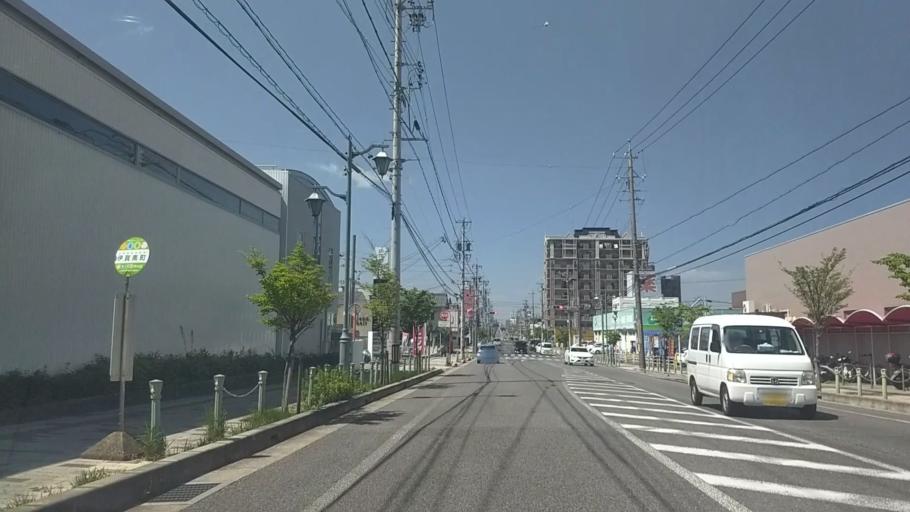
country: JP
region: Aichi
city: Okazaki
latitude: 34.9685
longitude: 137.1714
